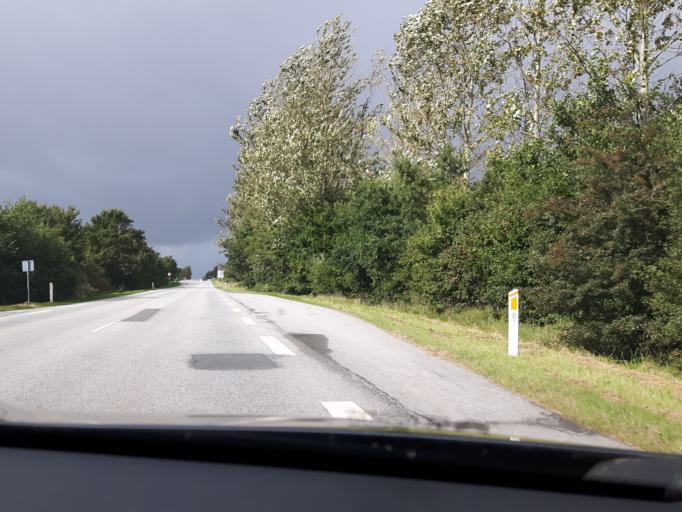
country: DK
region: North Denmark
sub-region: Jammerbugt Kommune
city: Fjerritslev
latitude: 57.0883
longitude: 9.3497
